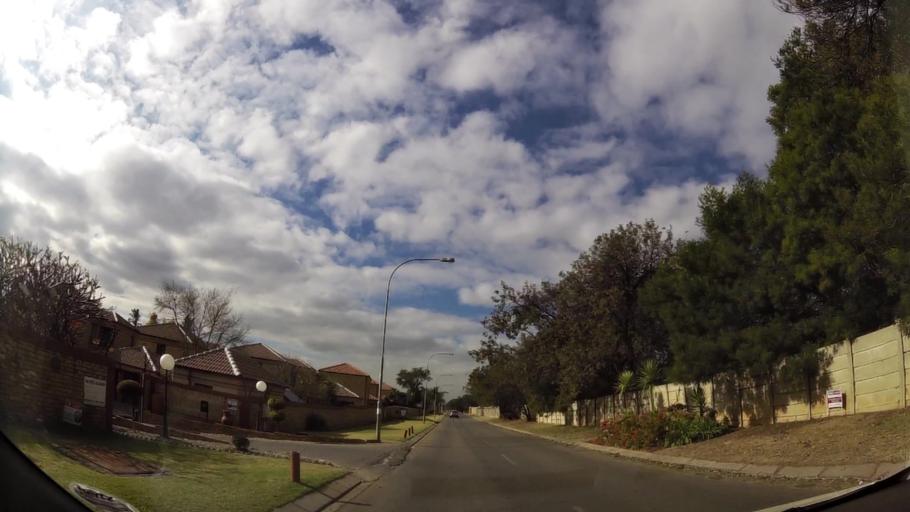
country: ZA
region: Gauteng
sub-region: City of Johannesburg Metropolitan Municipality
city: Roodepoort
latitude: -26.1017
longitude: 27.8765
